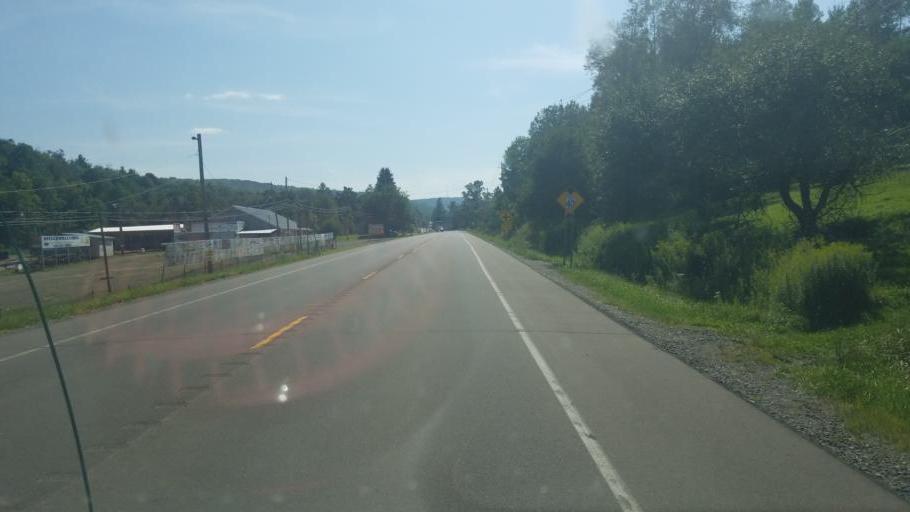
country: US
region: New York
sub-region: Allegany County
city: Bolivar
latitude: 42.0900
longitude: -78.0580
